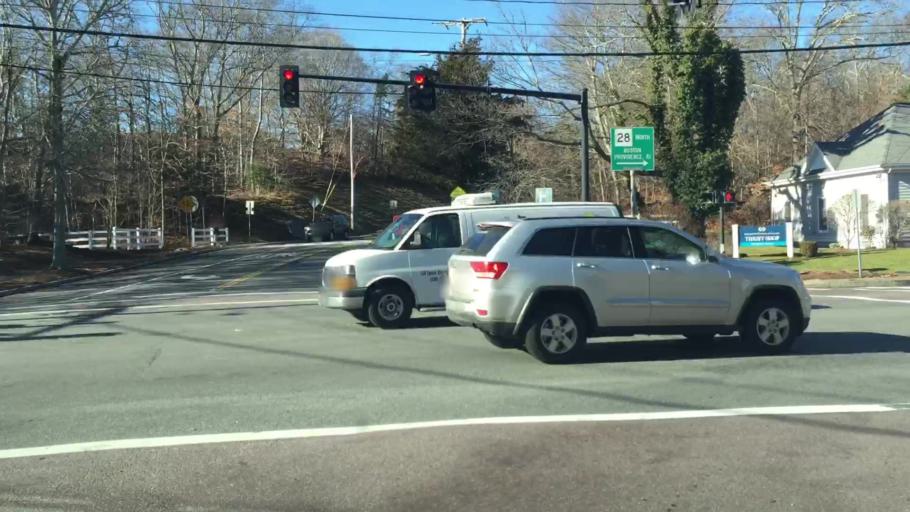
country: US
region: Massachusetts
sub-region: Barnstable County
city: Falmouth
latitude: 41.5641
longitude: -70.6186
